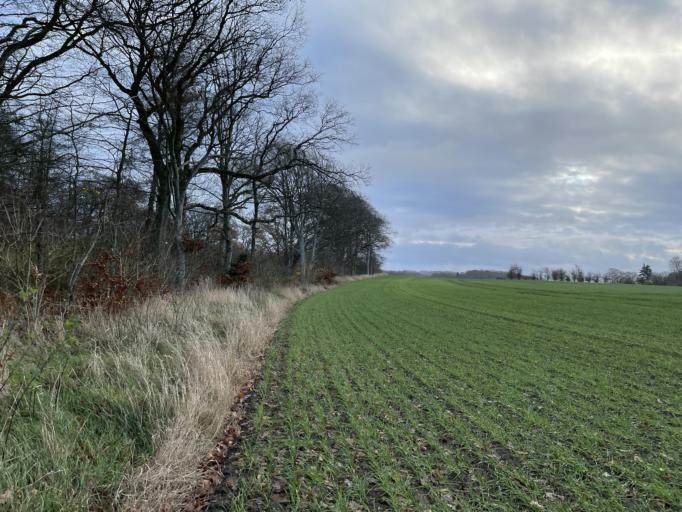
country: DK
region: Central Jutland
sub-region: Viborg Kommune
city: Bjerringbro
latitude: 56.2551
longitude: 9.6763
